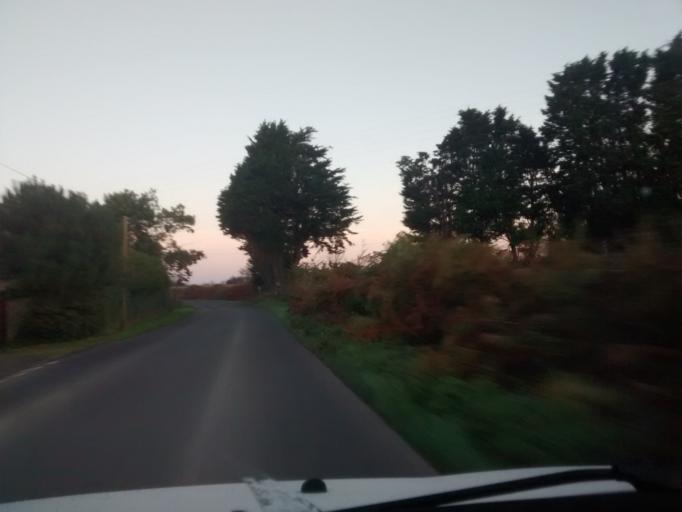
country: FR
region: Brittany
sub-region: Departement des Cotes-d'Armor
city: Trevou-Treguignec
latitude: 48.7927
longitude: -3.3451
